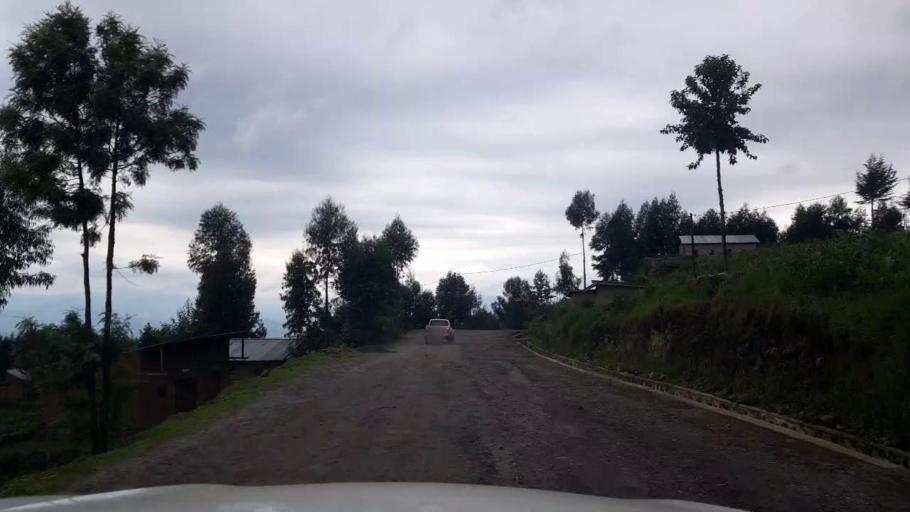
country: RW
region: Northern Province
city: Musanze
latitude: -1.4897
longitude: 29.5306
